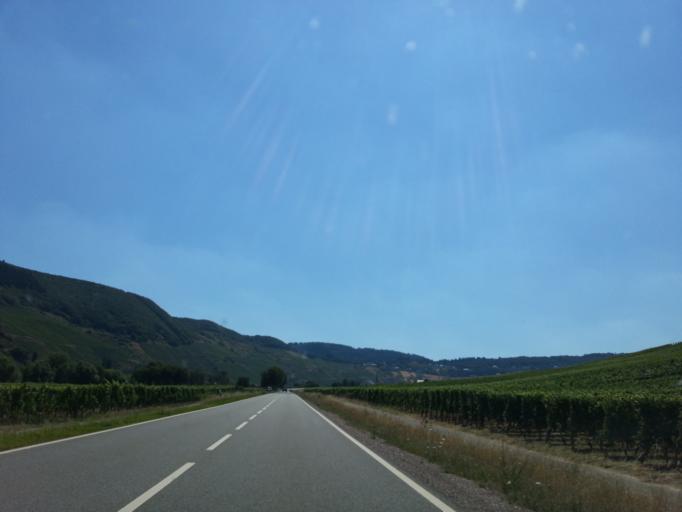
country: DE
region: Rheinland-Pfalz
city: Trittenheim
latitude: 49.8346
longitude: 6.8960
